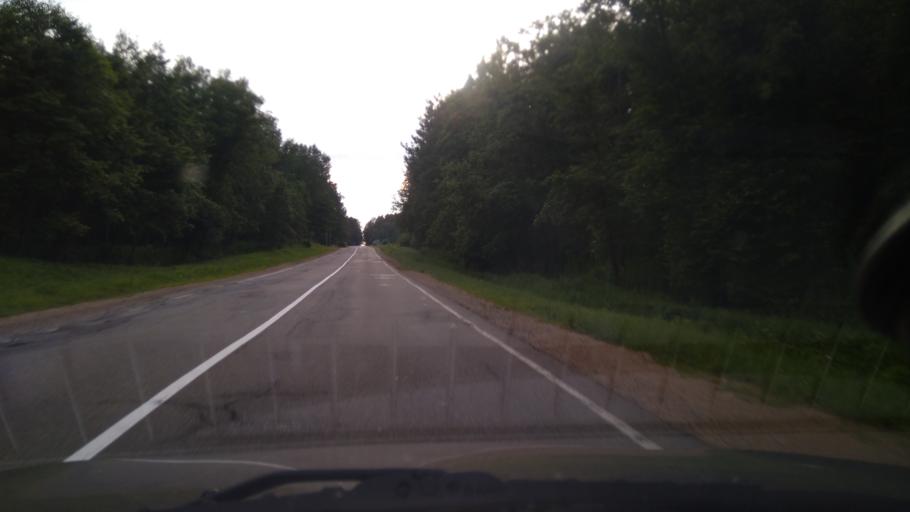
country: BY
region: Minsk
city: Bal'shavik
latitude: 53.9840
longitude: 27.5497
